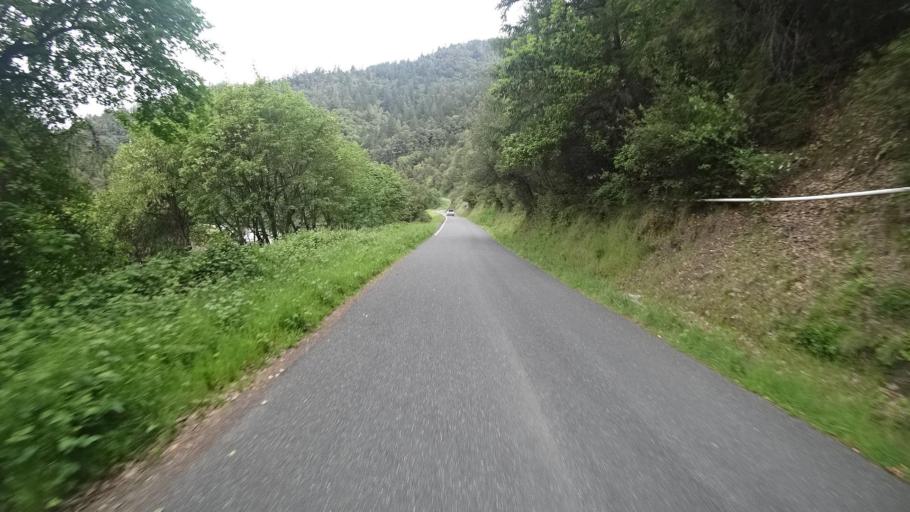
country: US
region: California
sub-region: Humboldt County
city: Willow Creek
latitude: 40.9454
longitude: -123.6110
